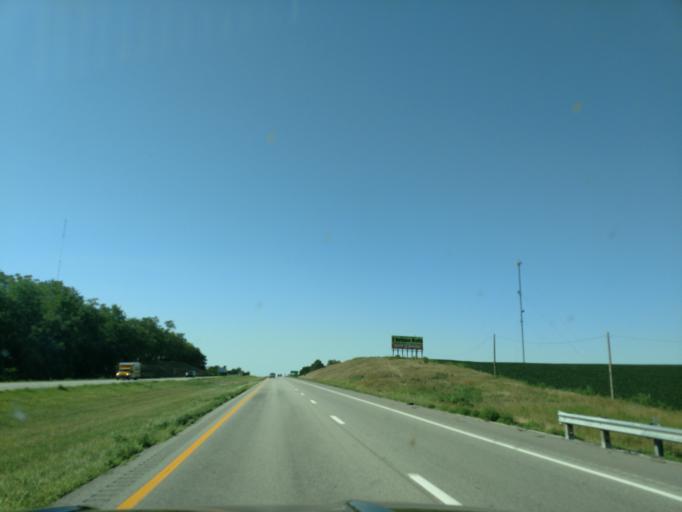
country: US
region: Missouri
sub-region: Andrew County
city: Country Club Village
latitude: 39.8241
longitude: -94.8053
